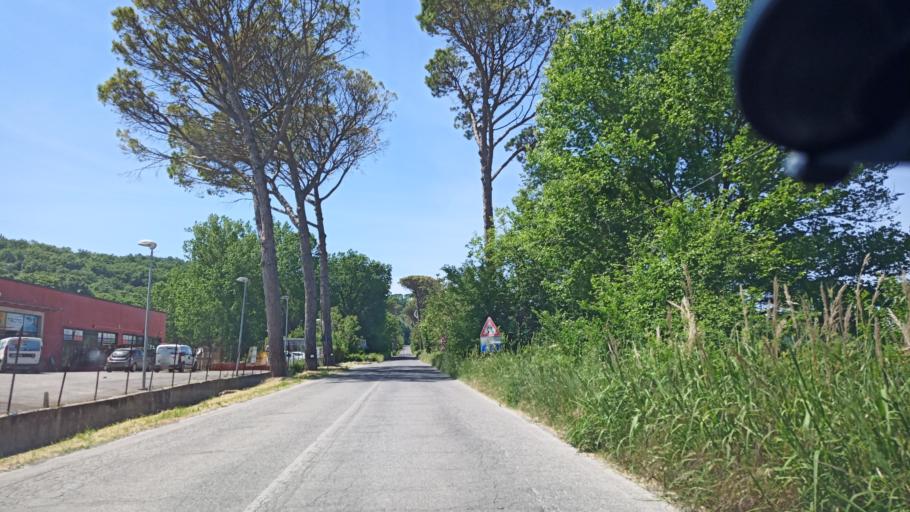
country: IT
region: Latium
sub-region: Provincia di Rieti
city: Stimigliano
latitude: 42.3125
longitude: 12.5748
